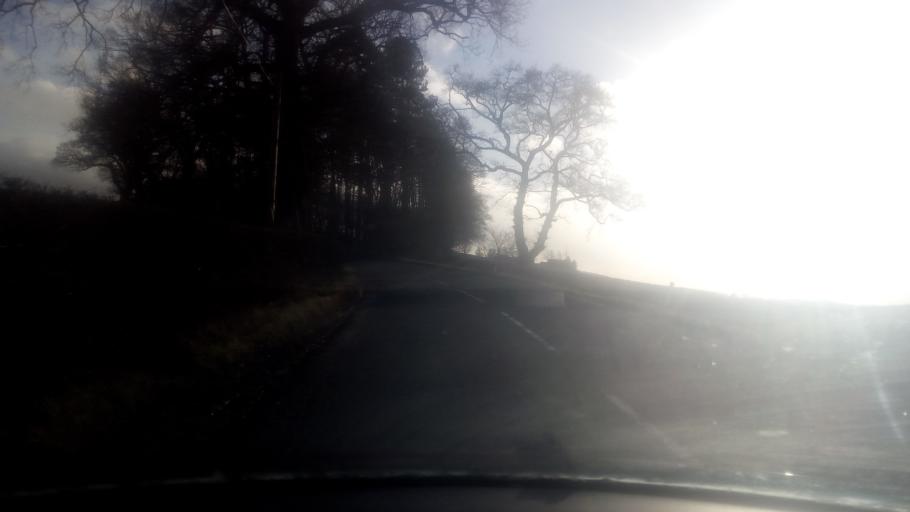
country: GB
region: Scotland
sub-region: The Scottish Borders
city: Kelso
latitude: 55.6616
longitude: -2.3827
